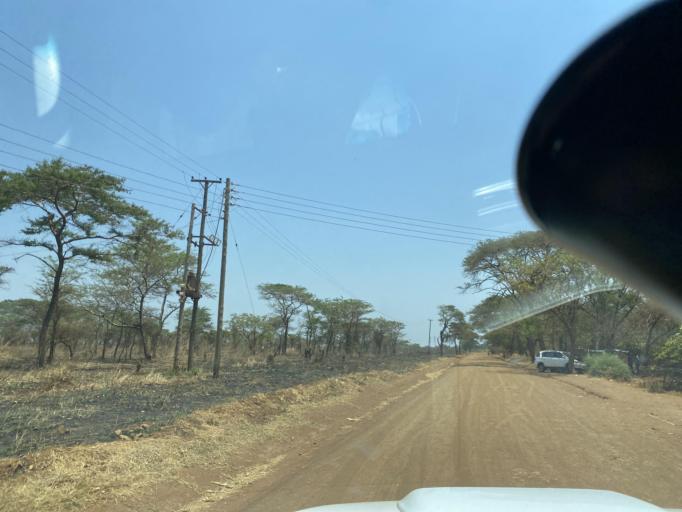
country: ZM
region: Lusaka
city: Lusaka
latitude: -15.4192
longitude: 28.1045
